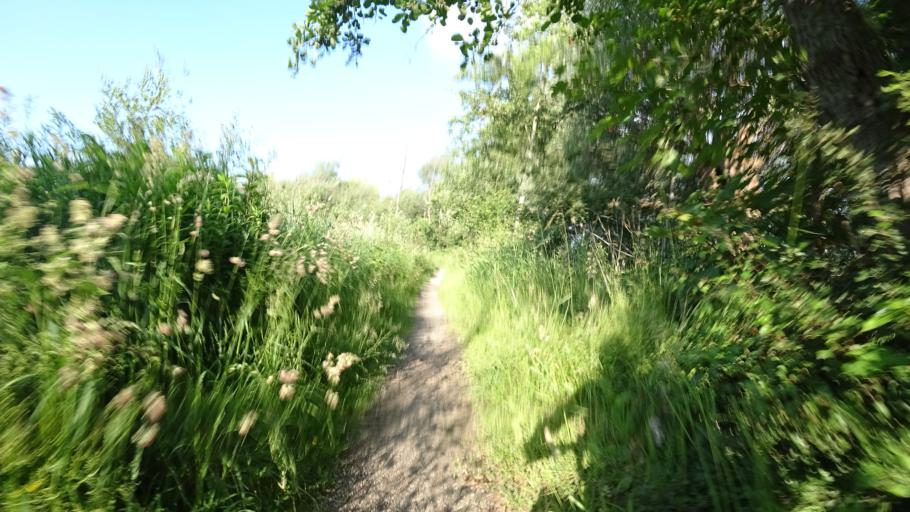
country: DE
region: North Rhine-Westphalia
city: Erwitte
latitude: 51.6356
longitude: 8.3740
